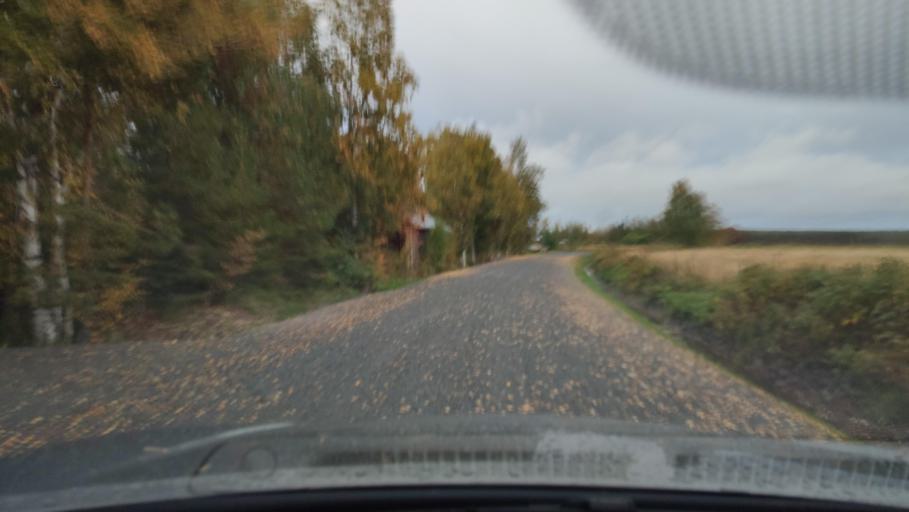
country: FI
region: Southern Ostrobothnia
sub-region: Suupohja
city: Karijoki
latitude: 62.2278
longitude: 21.6237
